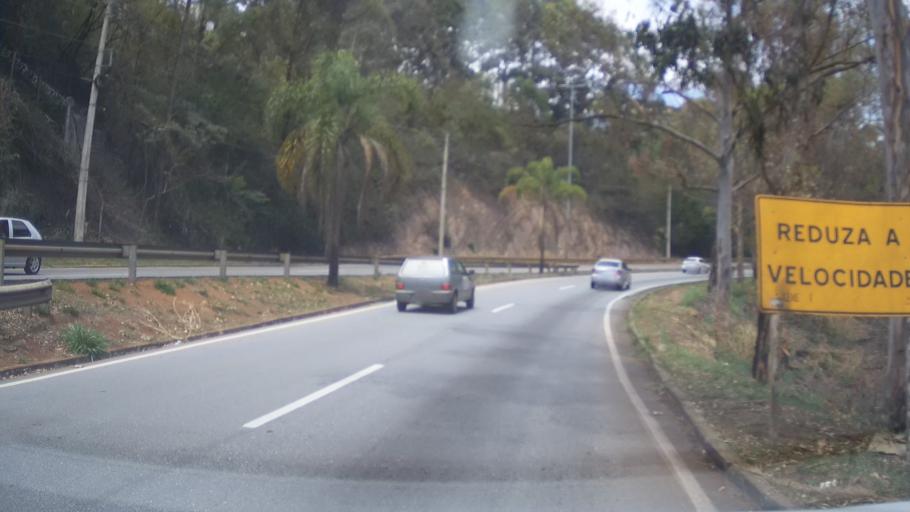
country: BR
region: Minas Gerais
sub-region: Belo Horizonte
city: Belo Horizonte
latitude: -19.9872
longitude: -43.9336
